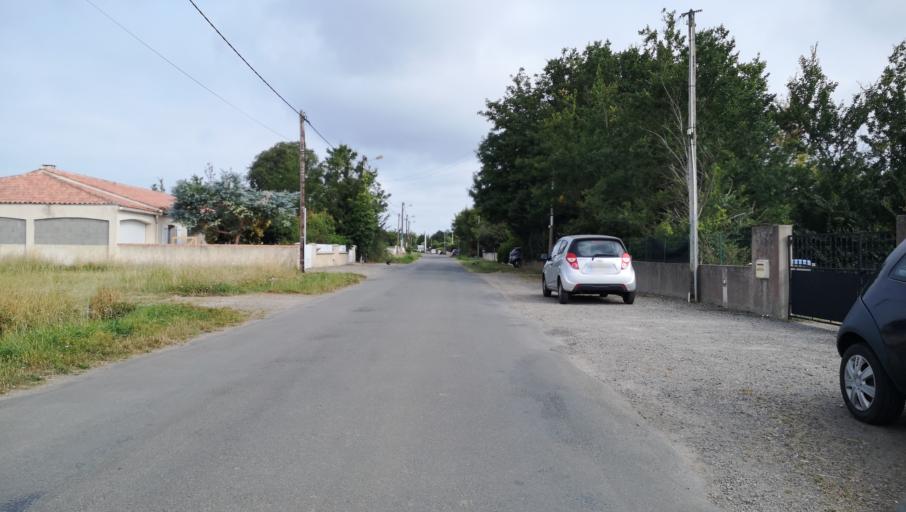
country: FR
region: Pays de la Loire
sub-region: Departement de la Vendee
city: Olonne-sur-Mer
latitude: 46.5517
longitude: -1.8037
